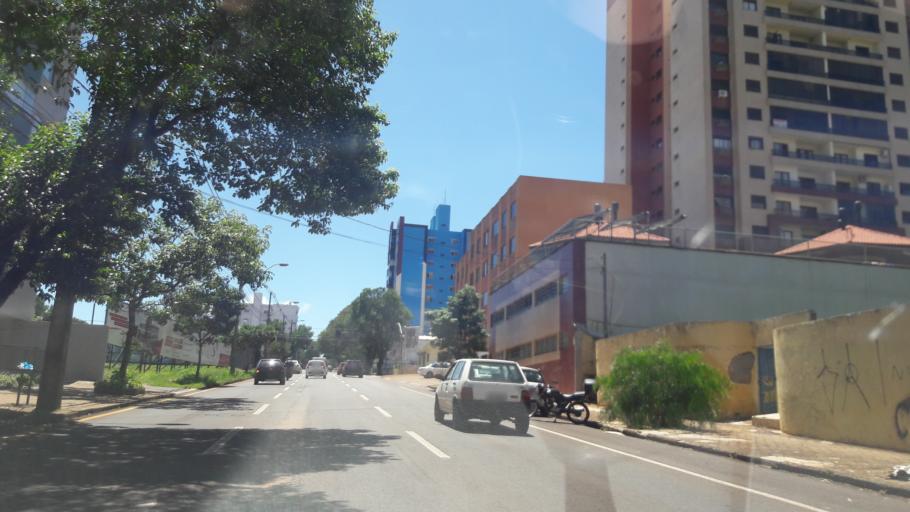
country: BR
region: Parana
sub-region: Cascavel
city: Cascavel
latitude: -24.9517
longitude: -53.4663
